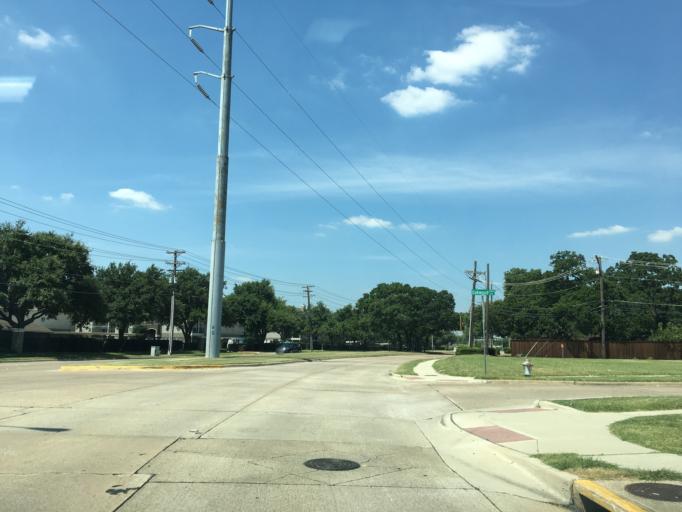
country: US
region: Texas
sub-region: Denton County
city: Lewisville
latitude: 33.0275
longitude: -96.9962
